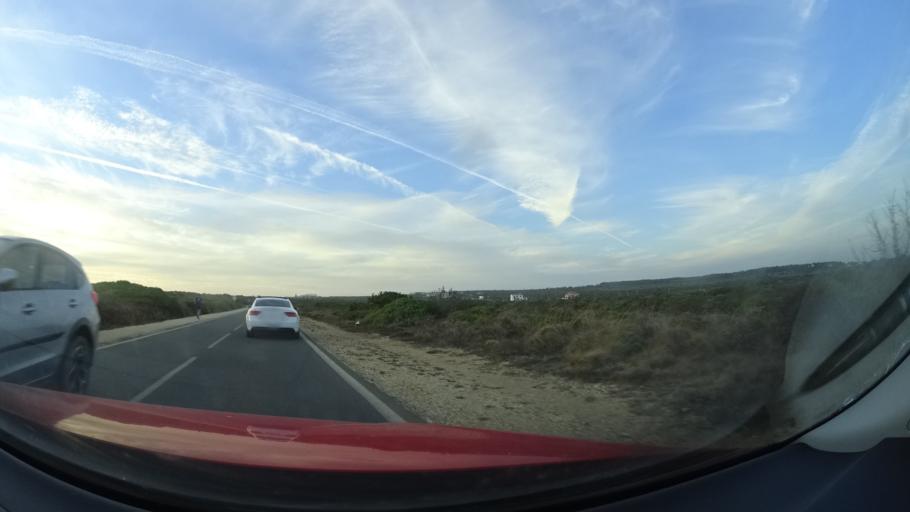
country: PT
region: Faro
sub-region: Vila do Bispo
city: Sagres
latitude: 37.0133
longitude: -8.9526
